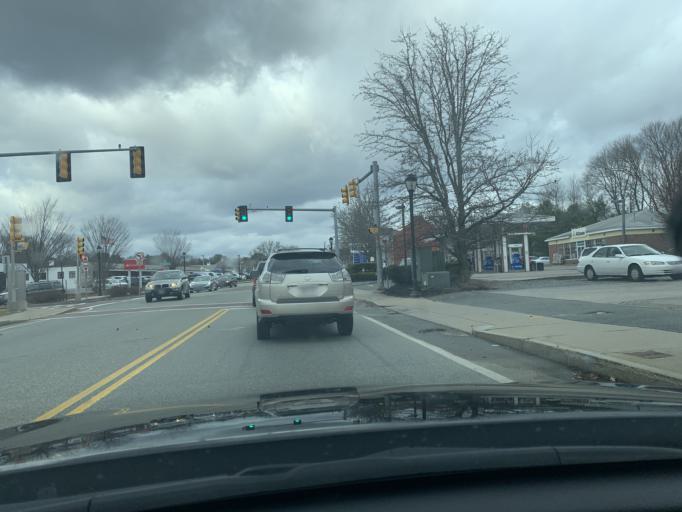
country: US
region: Massachusetts
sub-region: Norfolk County
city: Westwood
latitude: 42.2237
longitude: -71.2229
